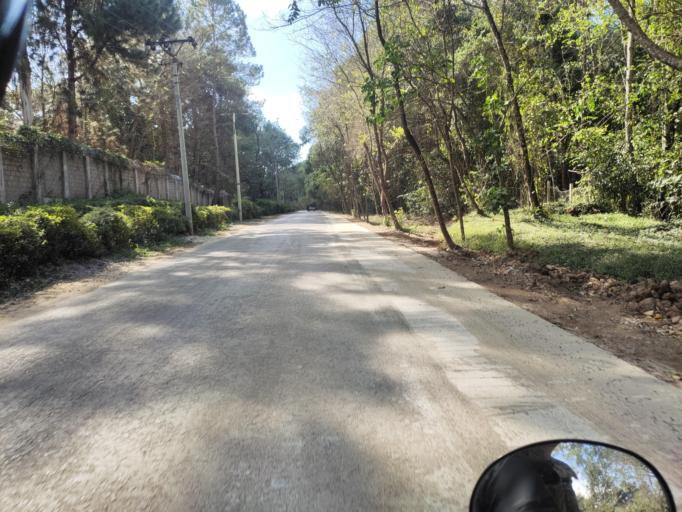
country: MM
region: Mandalay
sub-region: Pyin Oo Lwin District
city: Pyin Oo Lwin
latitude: 21.9905
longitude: 96.4720
